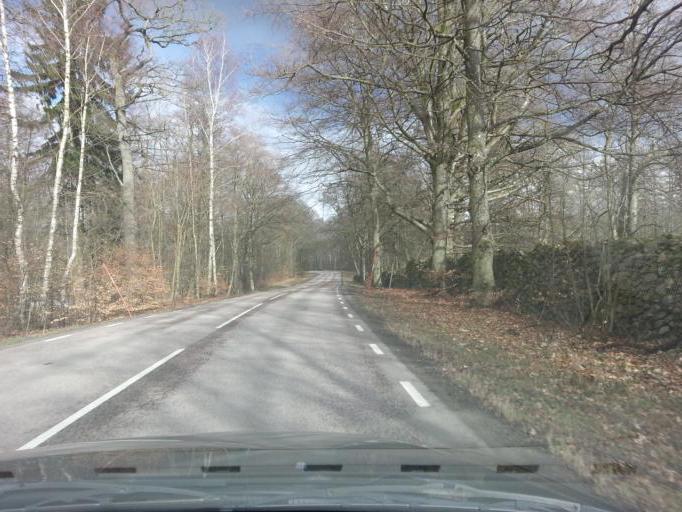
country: SE
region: Skane
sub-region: Astorps Kommun
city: Astorp
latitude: 56.1113
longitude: 12.9795
